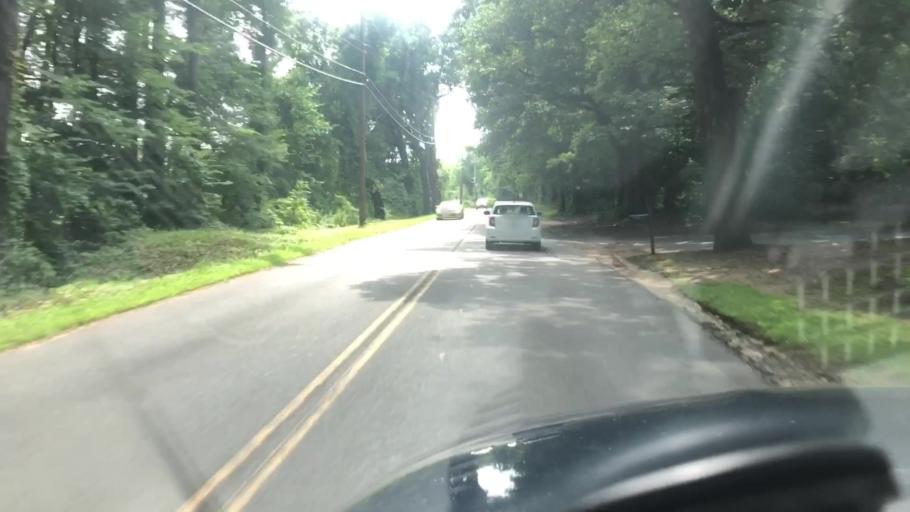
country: US
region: Massachusetts
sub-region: Hampden County
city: Westfield
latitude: 42.1169
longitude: -72.7000
